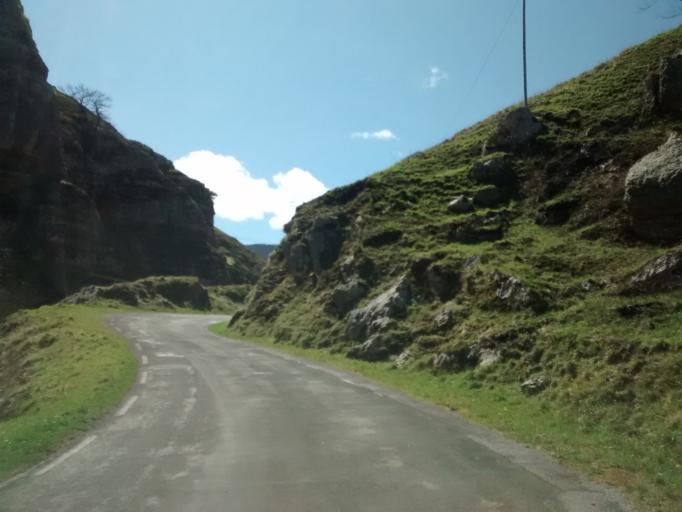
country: ES
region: Cantabria
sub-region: Provincia de Cantabria
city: Selaya
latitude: 43.2238
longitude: -3.7074
